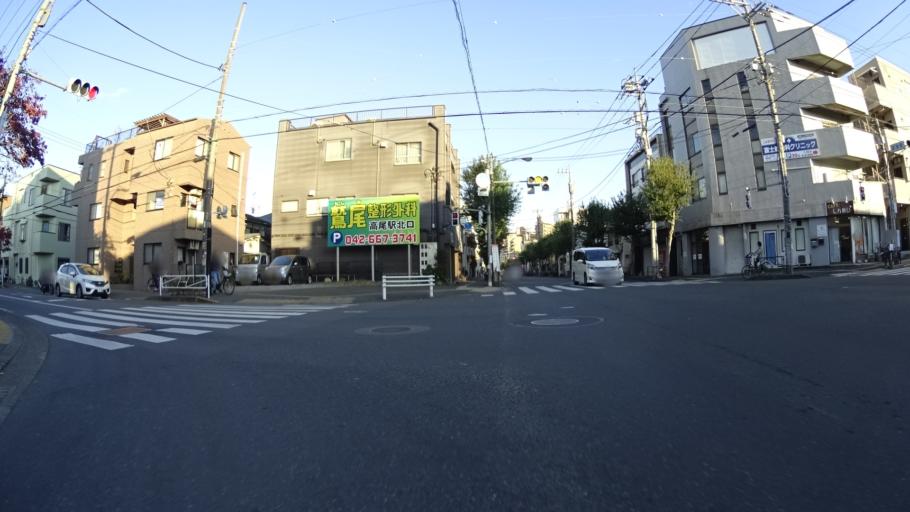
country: JP
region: Tokyo
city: Hachioji
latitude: 35.6616
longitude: 139.3138
